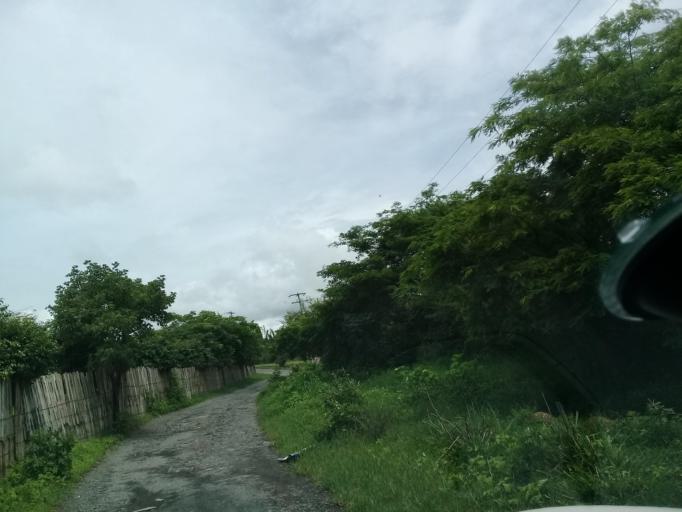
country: MX
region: Veracruz
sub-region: Emiliano Zapata
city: Dos Rios
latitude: 19.4698
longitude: -96.7754
